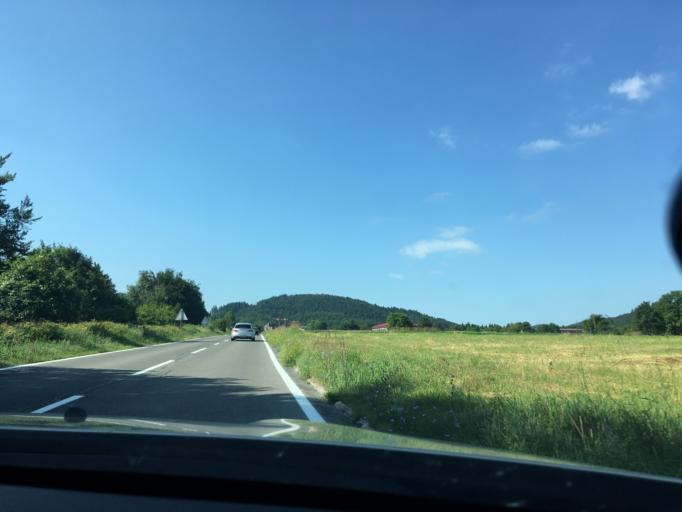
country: HR
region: Primorsko-Goranska
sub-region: Grad Delnice
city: Delnice
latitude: 45.4007
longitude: 14.8090
